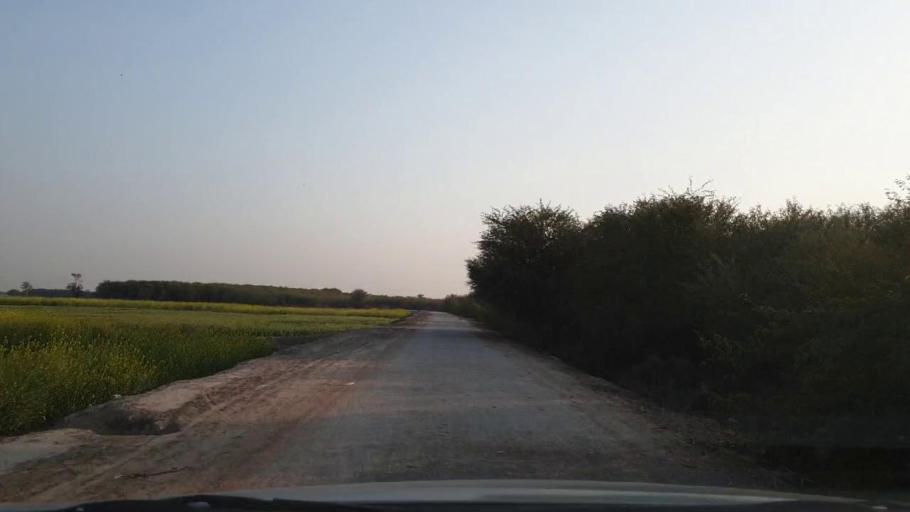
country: PK
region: Sindh
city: Tando Adam
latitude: 25.7156
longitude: 68.5944
